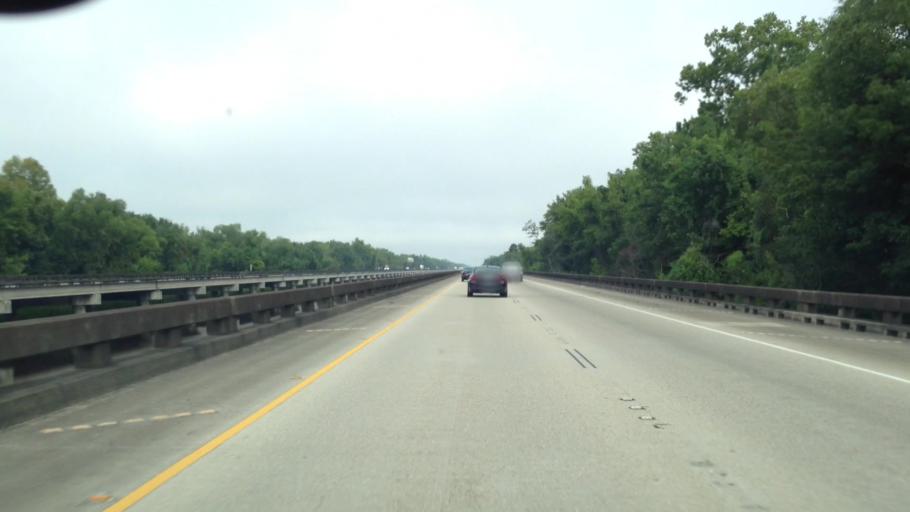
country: US
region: Louisiana
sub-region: Saint John the Baptist Parish
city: Montegut
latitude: 30.1087
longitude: -90.5161
